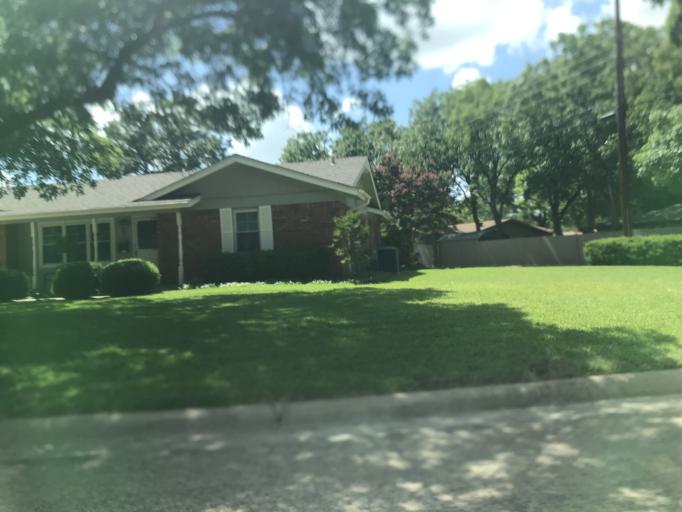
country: US
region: Texas
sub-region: Taylor County
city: Abilene
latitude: 32.4220
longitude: -99.7607
